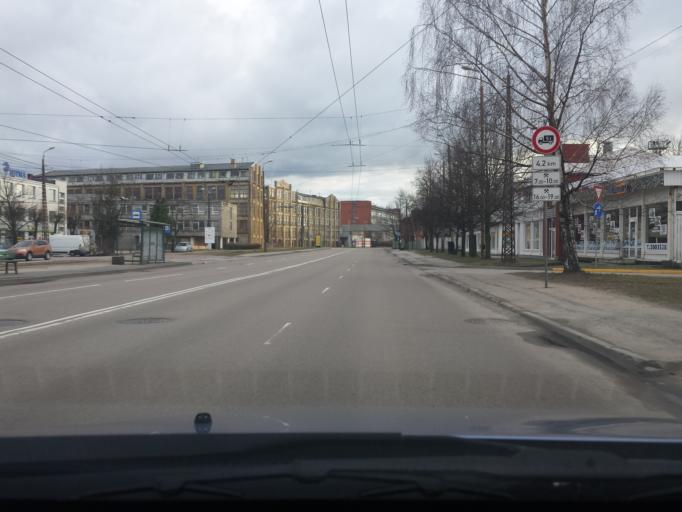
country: LV
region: Riga
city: Riga
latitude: 56.9879
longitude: 24.1214
